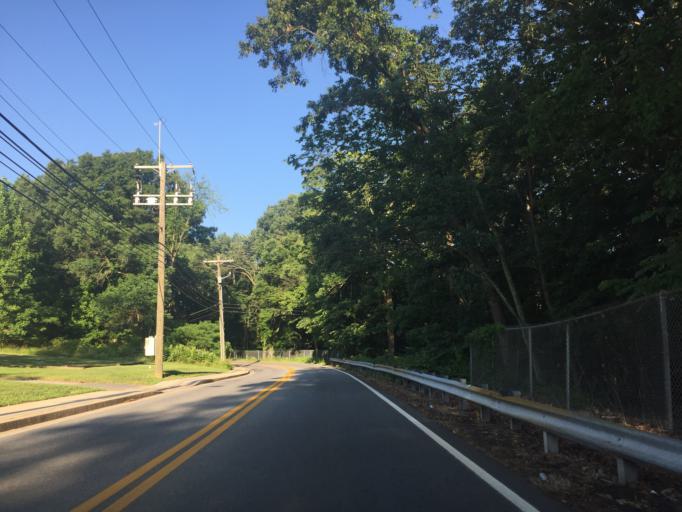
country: US
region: Maryland
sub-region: Baltimore County
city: Arbutus
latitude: 39.2458
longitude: -76.7100
